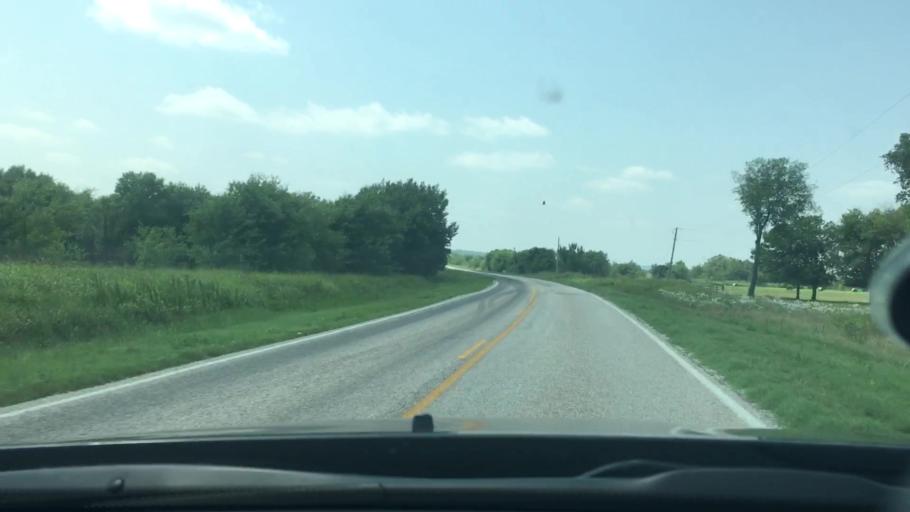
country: US
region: Oklahoma
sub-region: Johnston County
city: Tishomingo
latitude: 34.3760
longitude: -96.4677
